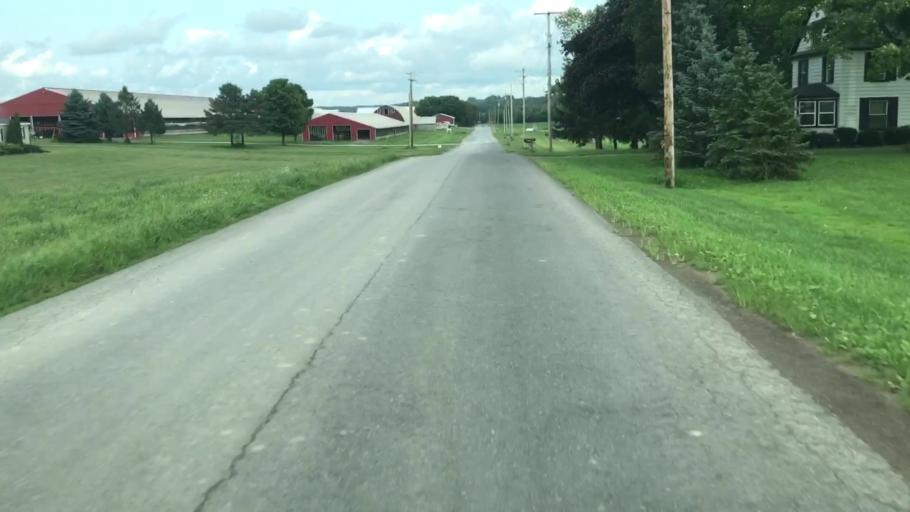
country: US
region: New York
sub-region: Onondaga County
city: Elbridge
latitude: 42.9859
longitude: -76.4715
